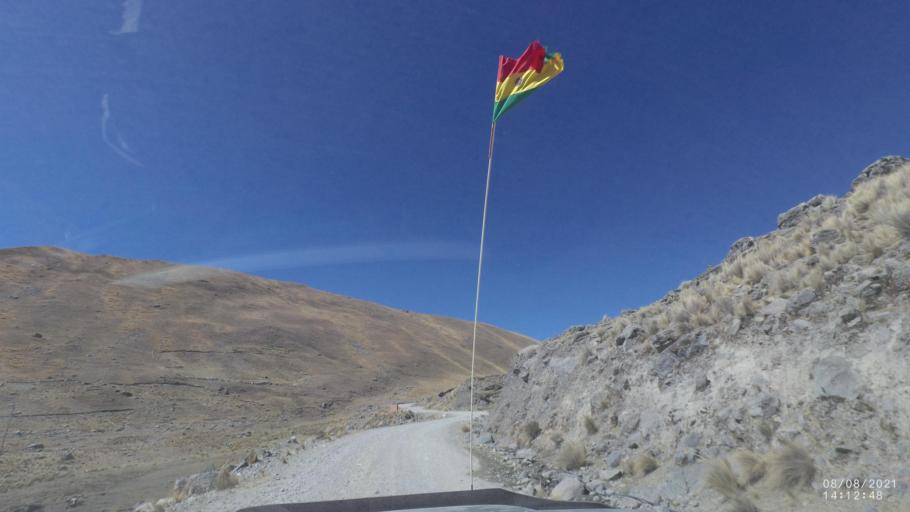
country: BO
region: Cochabamba
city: Sipe Sipe
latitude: -17.1654
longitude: -66.4264
